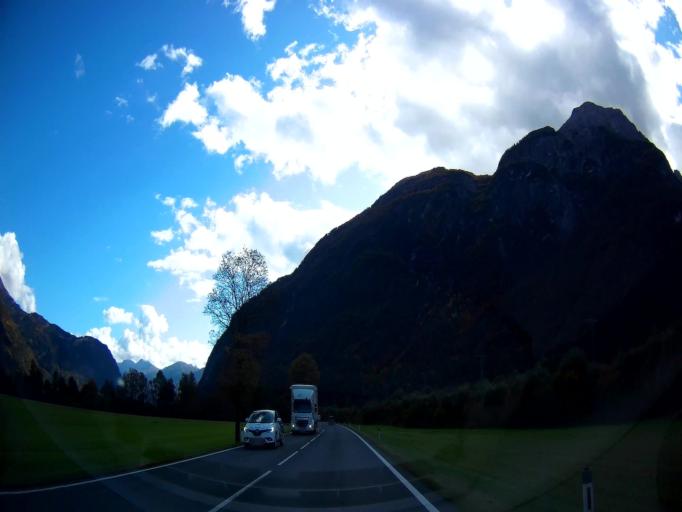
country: AT
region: Tyrol
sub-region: Politischer Bezirk Lienz
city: Nikolsdorf
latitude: 46.7902
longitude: 12.8766
